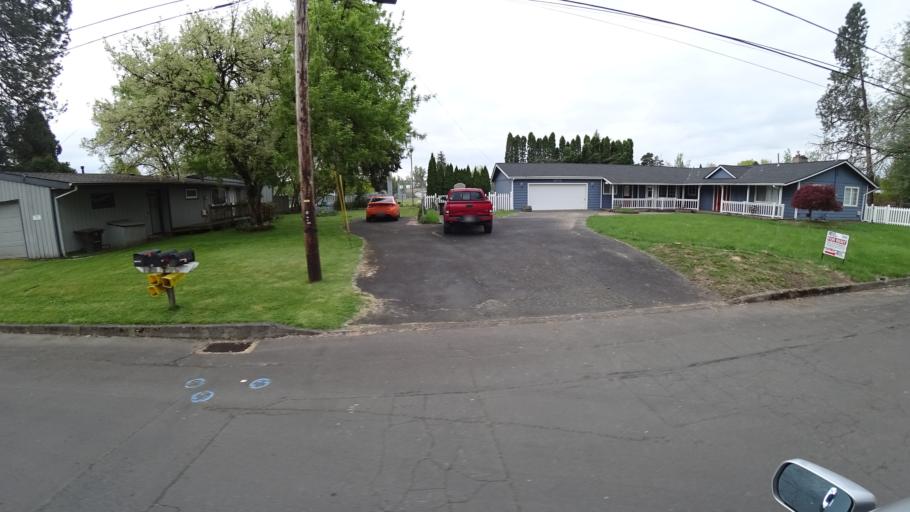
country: US
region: Oregon
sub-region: Washington County
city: Hillsboro
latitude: 45.5346
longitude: -122.9701
